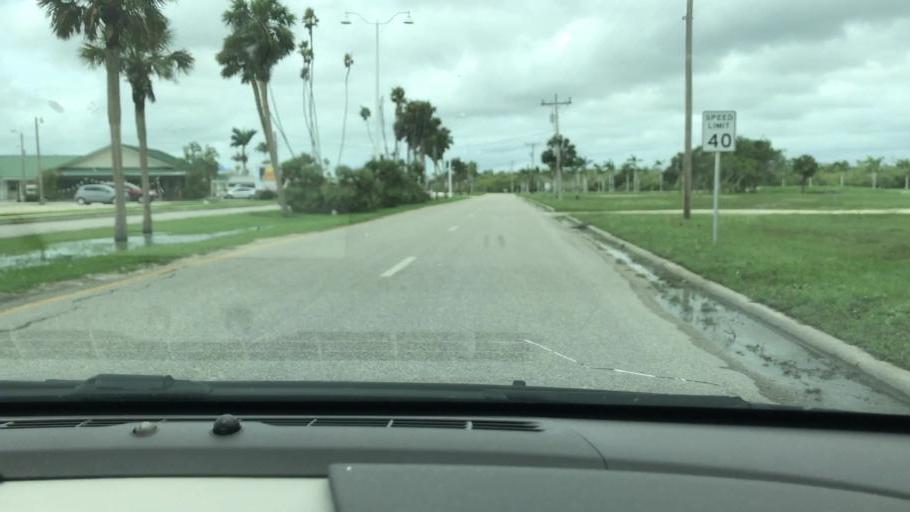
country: US
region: Florida
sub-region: Collier County
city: Marco
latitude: 25.8600
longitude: -81.3829
